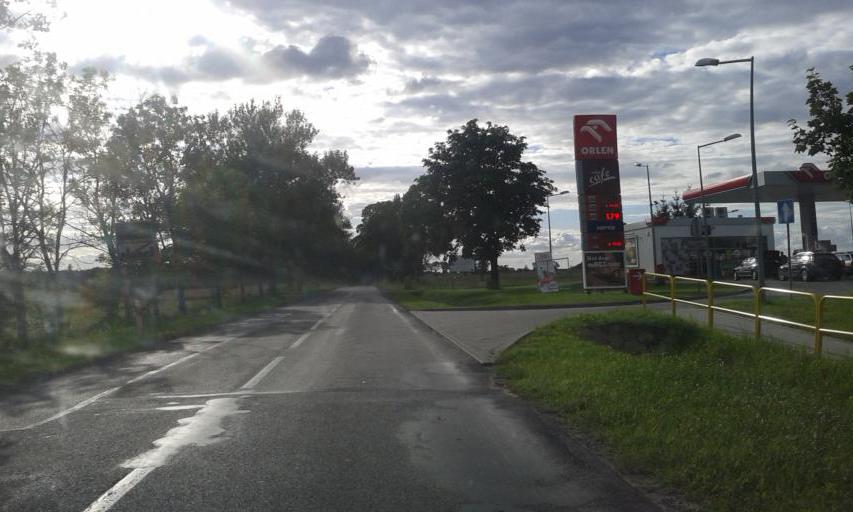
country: PL
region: West Pomeranian Voivodeship
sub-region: Powiat bialogardzki
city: Tychowo
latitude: 53.9264
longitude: 16.2484
